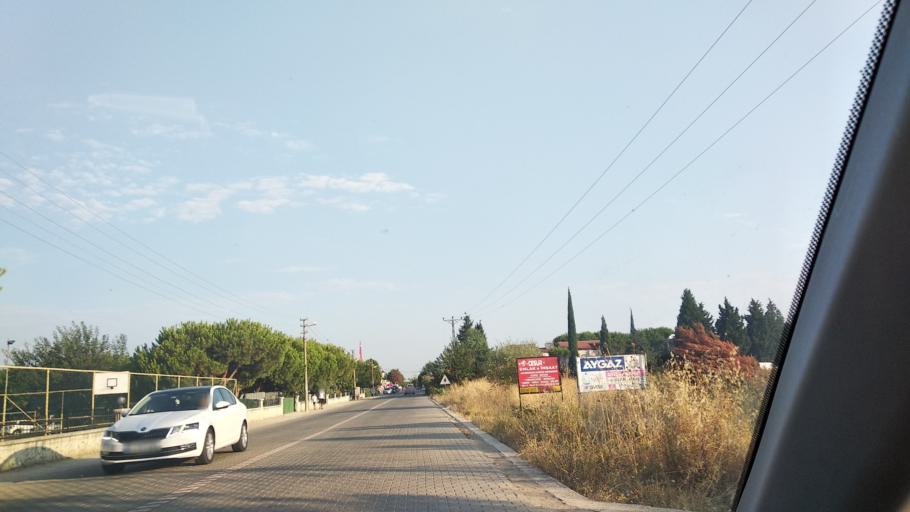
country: TR
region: Balikesir
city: Altinova
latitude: 39.1565
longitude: 26.8242
